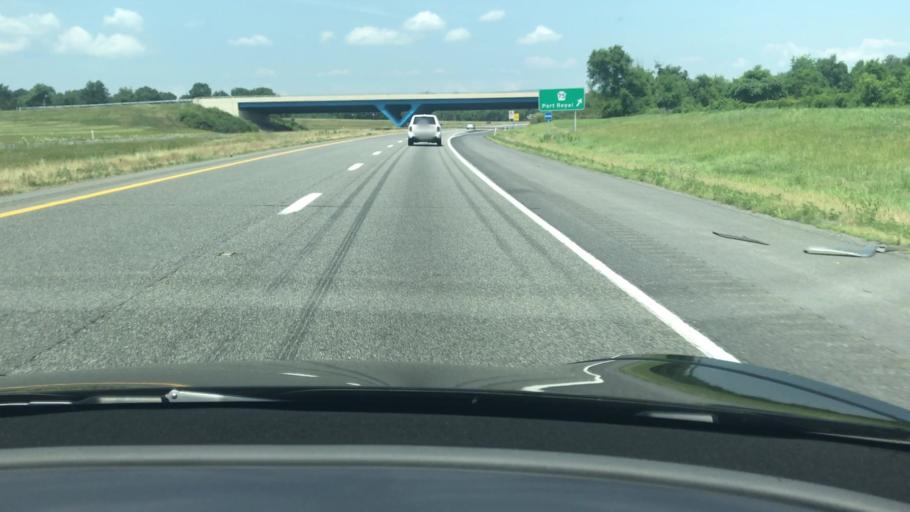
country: US
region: Pennsylvania
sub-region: Juniata County
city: Mifflintown
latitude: 40.5539
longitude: -77.3599
